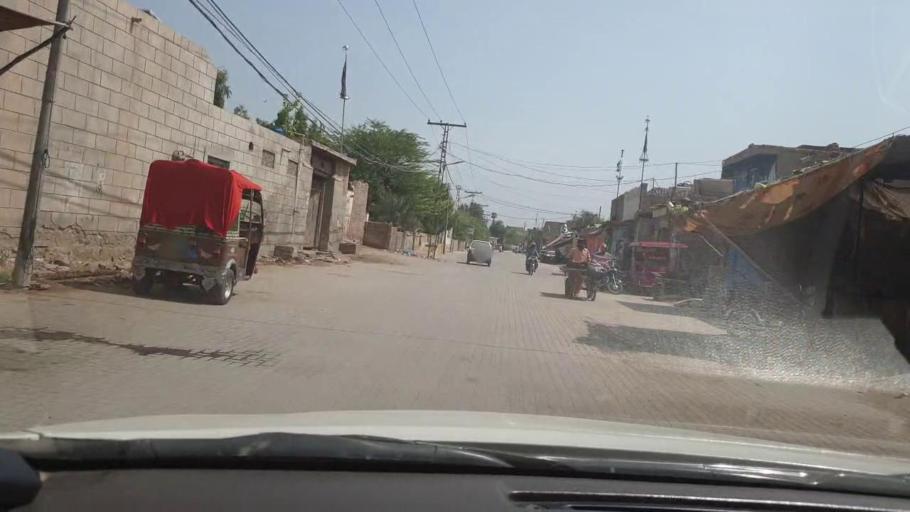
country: PK
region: Sindh
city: Shikarpur
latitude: 27.9518
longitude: 68.6290
